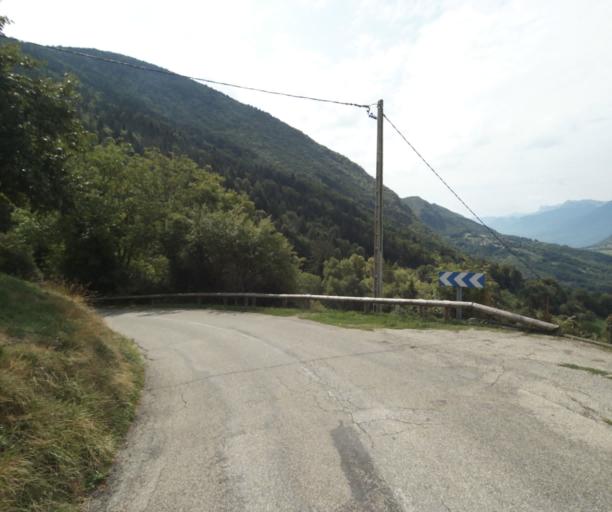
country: FR
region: Rhone-Alpes
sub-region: Departement de l'Isere
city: Le Sappey-en-Chartreuse
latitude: 45.2627
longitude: 5.7484
